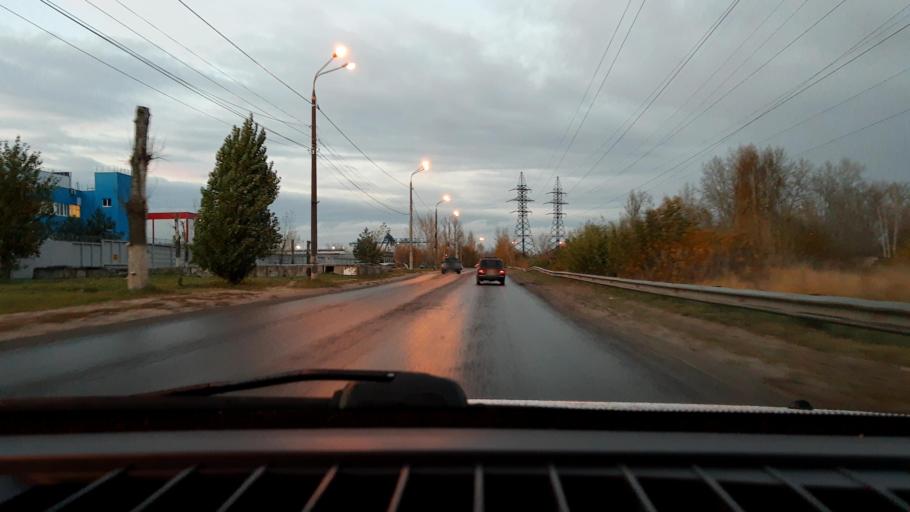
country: RU
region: Nizjnij Novgorod
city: Gorbatovka
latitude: 56.3705
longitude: 43.7983
